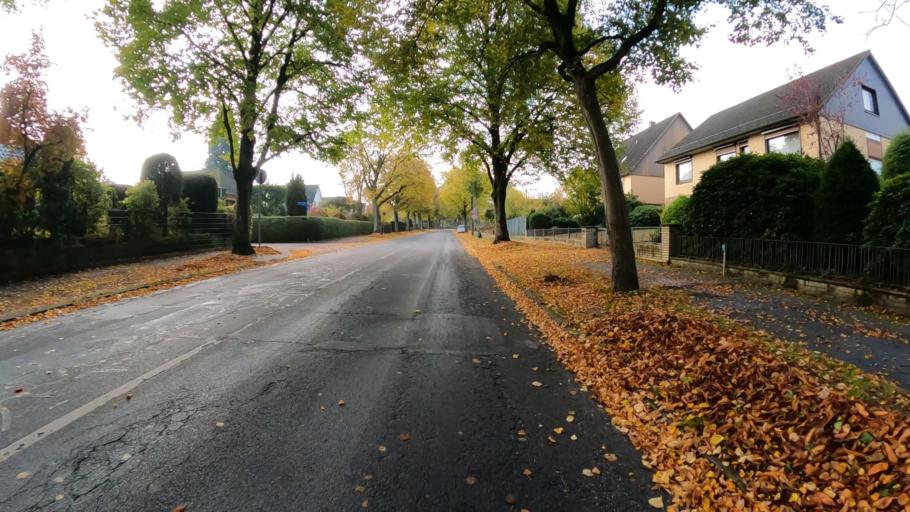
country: DE
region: Schleswig-Holstein
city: Ahrensburg
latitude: 53.6570
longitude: 10.2355
